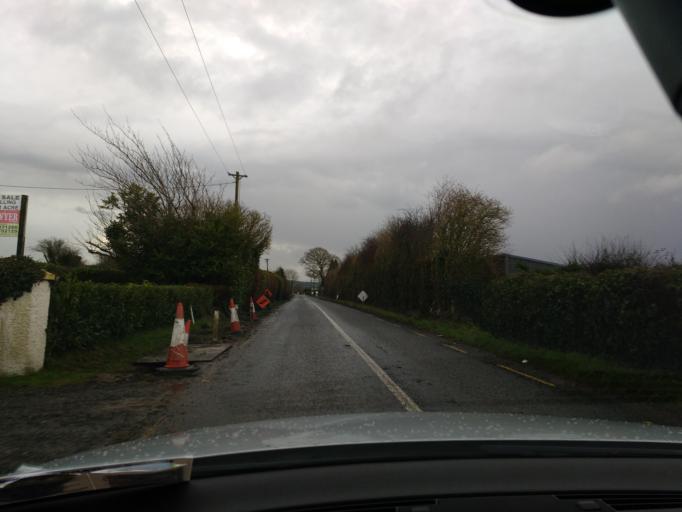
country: IE
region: Leinster
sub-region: Laois
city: Rathdowney
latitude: 52.6953
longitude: -7.5866
